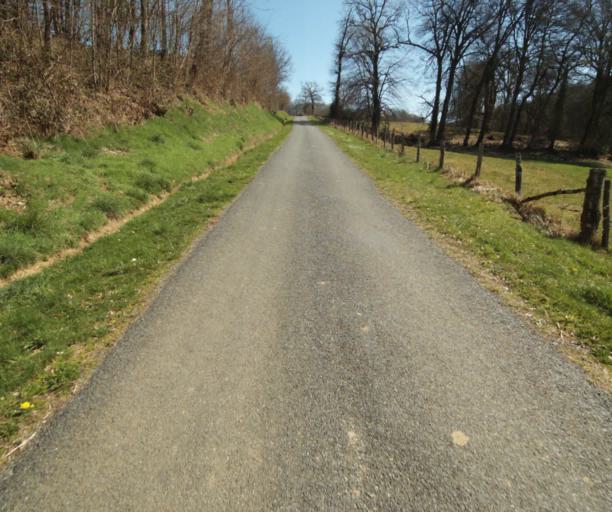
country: FR
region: Limousin
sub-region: Departement de la Correze
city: Uzerche
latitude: 45.3997
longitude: 1.6195
